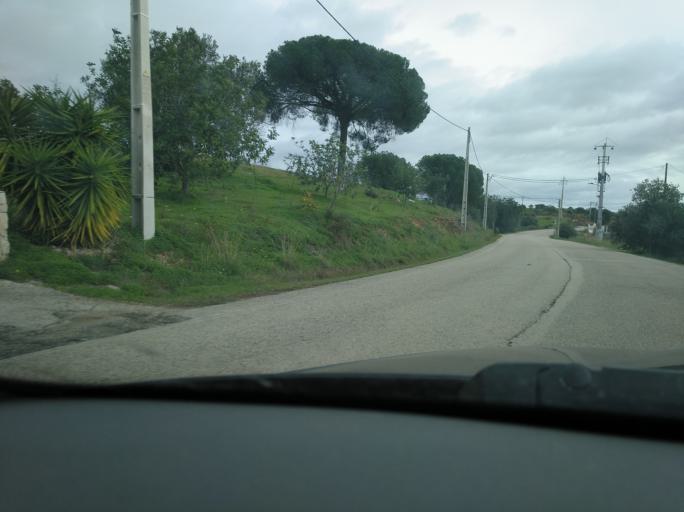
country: PT
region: Faro
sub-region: Castro Marim
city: Castro Marim
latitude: 37.2257
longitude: -7.4881
